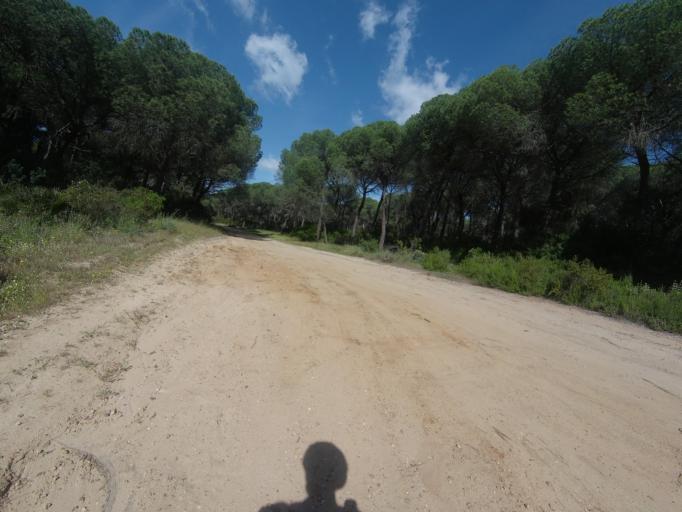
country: ES
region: Andalusia
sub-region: Provincia de Huelva
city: Aljaraque
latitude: 37.2355
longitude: -7.0506
